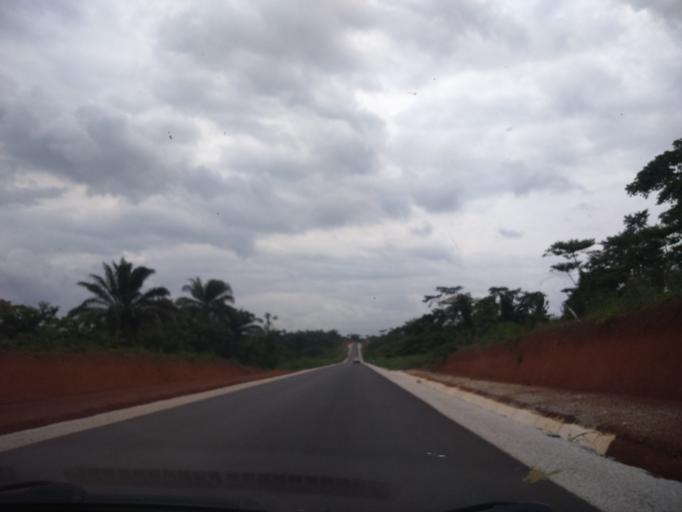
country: CI
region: Lagunes
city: Akoupe
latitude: 6.3275
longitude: -3.8402
